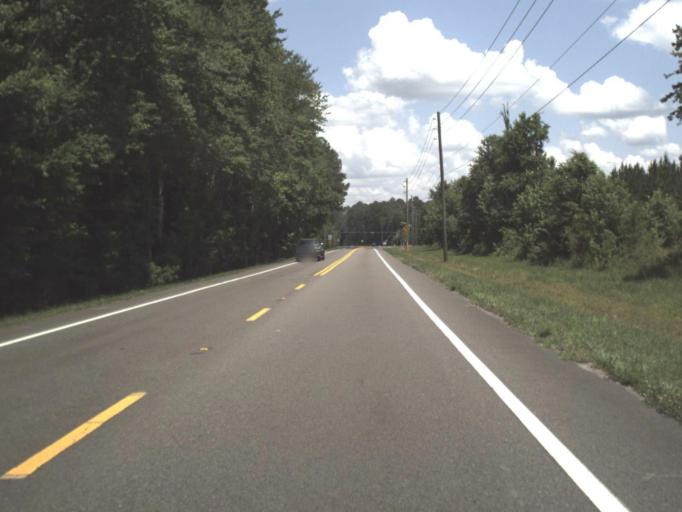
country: US
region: Florida
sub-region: Nassau County
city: Nassau Village-Ratliff
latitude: 30.4714
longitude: -81.7097
